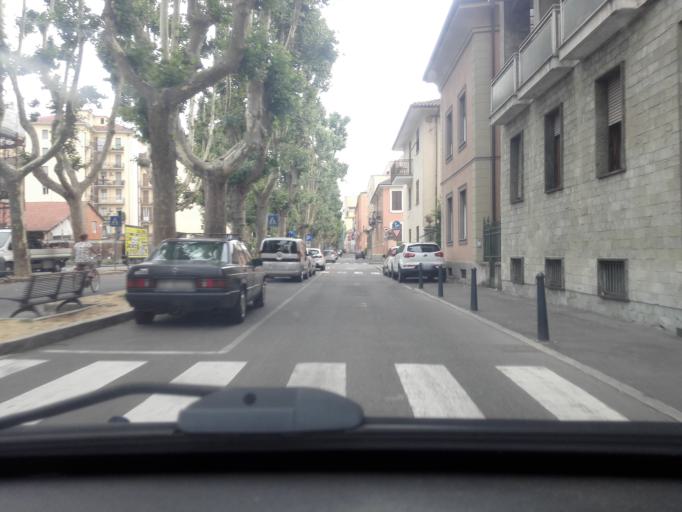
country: IT
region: Piedmont
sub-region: Provincia di Alessandria
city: Novi Ligure
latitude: 44.7666
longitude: 8.7892
